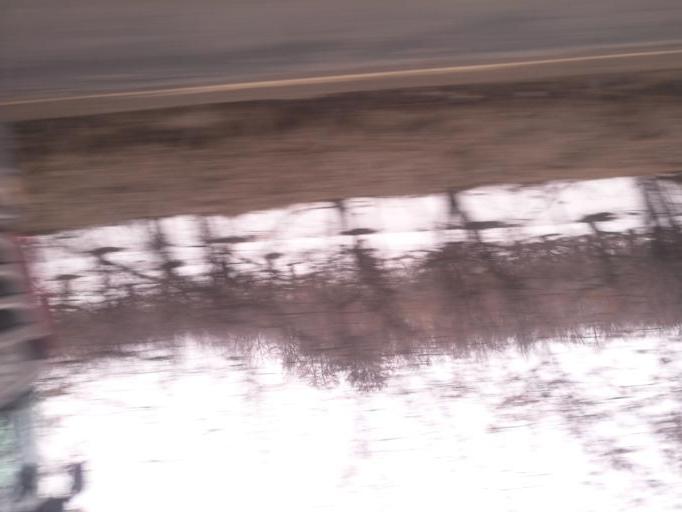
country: RO
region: Suceava
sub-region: Municipiul Falticeni
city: Falticeni
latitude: 47.4388
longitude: 26.2968
